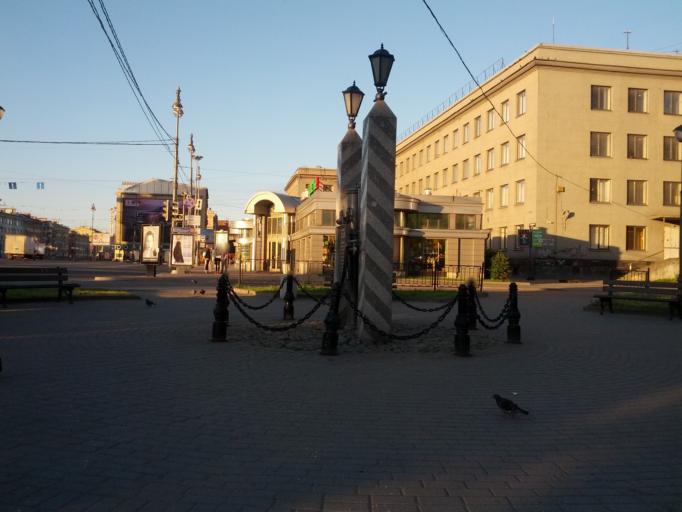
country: RU
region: St.-Petersburg
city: Admiralteisky
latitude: 59.8924
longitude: 30.3184
